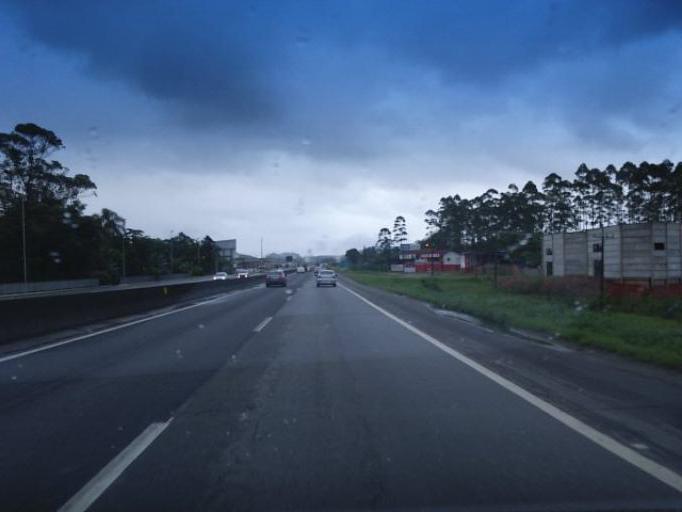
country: BR
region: Santa Catarina
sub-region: Barra Velha
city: Barra Velha
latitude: -26.6255
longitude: -48.7118
